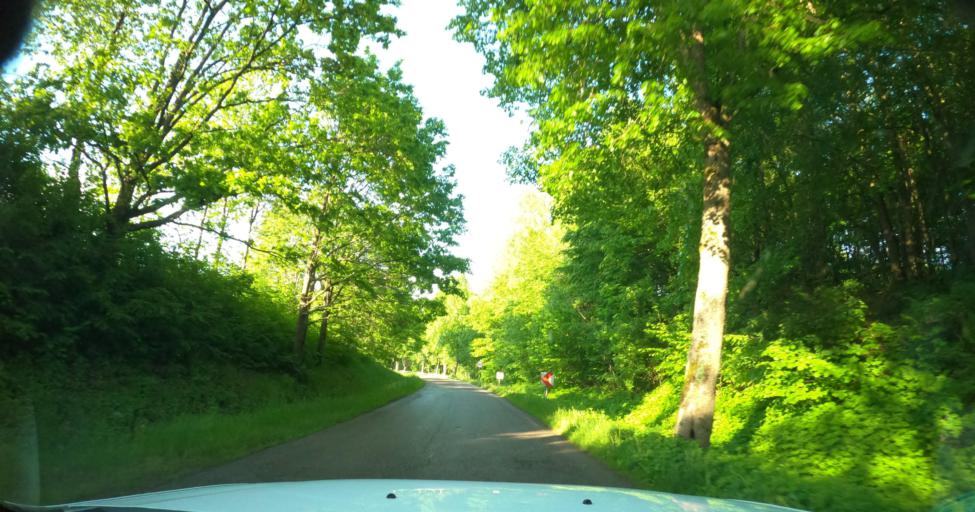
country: PL
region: Warmian-Masurian Voivodeship
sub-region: Powiat braniewski
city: Braniewo
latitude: 54.2792
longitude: 19.8471
